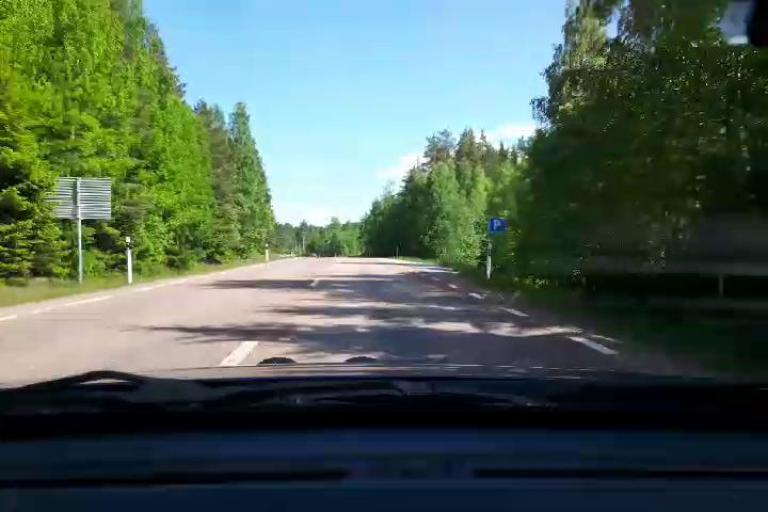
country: SE
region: Gaevleborg
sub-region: Hudiksvalls Kommun
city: Delsbo
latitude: 61.8026
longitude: 16.4731
